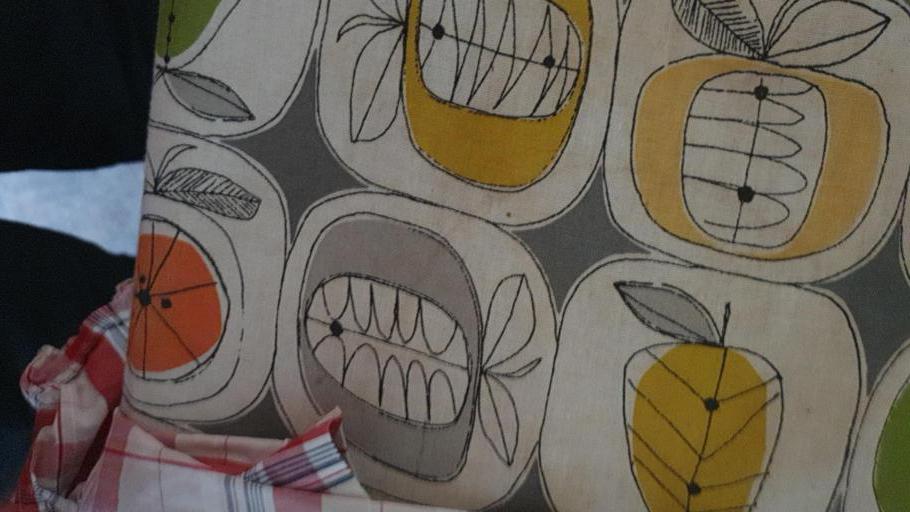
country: SE
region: Kalmar
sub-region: Torsas Kommun
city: Torsas
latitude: 56.4743
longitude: 16.0903
